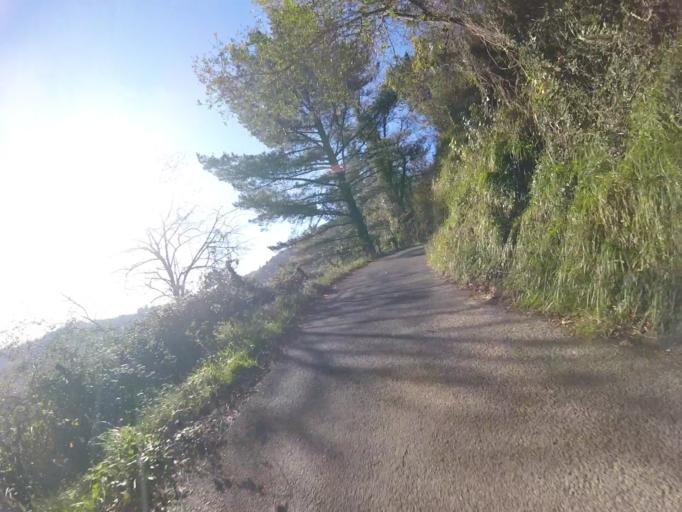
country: ES
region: Basque Country
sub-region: Provincia de Guipuzcoa
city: Usurbil
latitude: 43.2998
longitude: -2.0530
